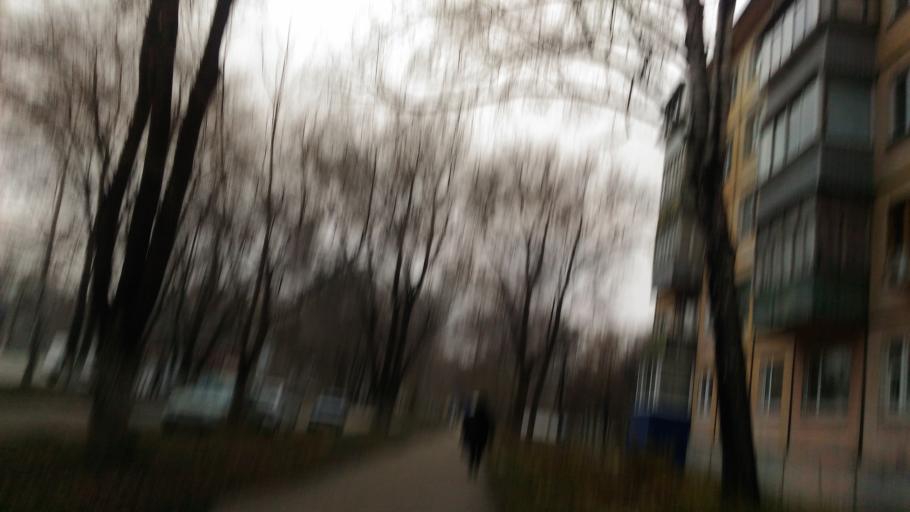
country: RU
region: Ulyanovsk
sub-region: Ulyanovskiy Rayon
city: Ulyanovsk
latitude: 54.2989
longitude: 48.3237
